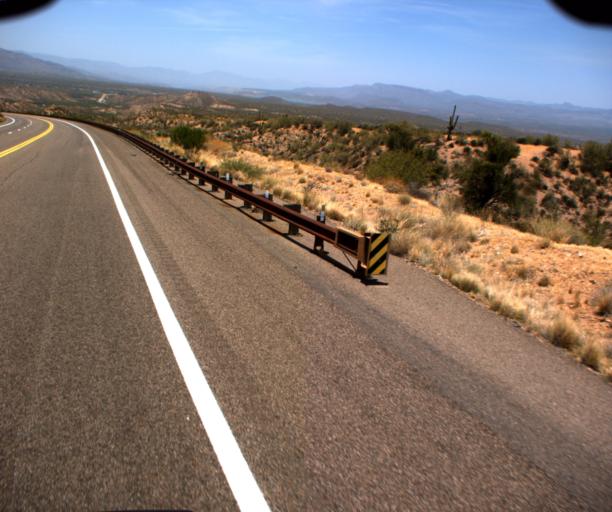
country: US
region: Arizona
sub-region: Gila County
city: Miami
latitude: 33.5801
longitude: -110.9644
